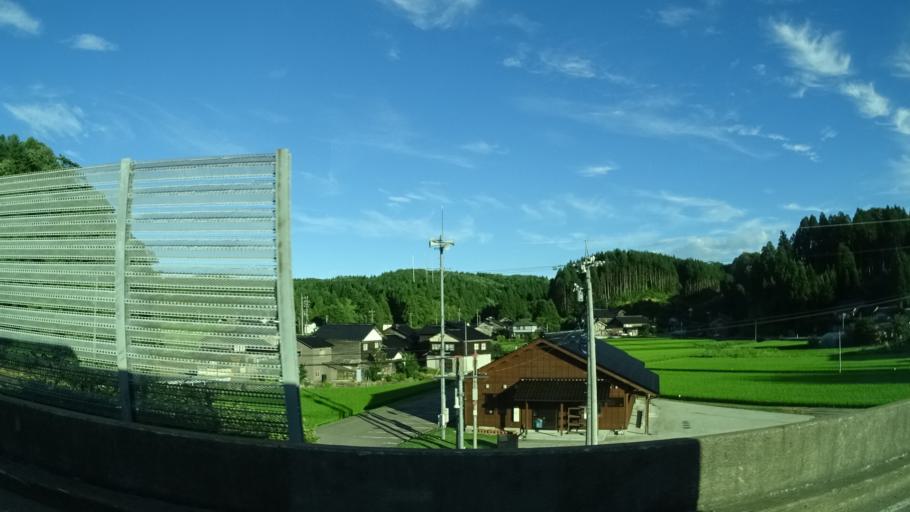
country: JP
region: Ishikawa
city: Nanao
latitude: 37.2948
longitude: 136.8952
